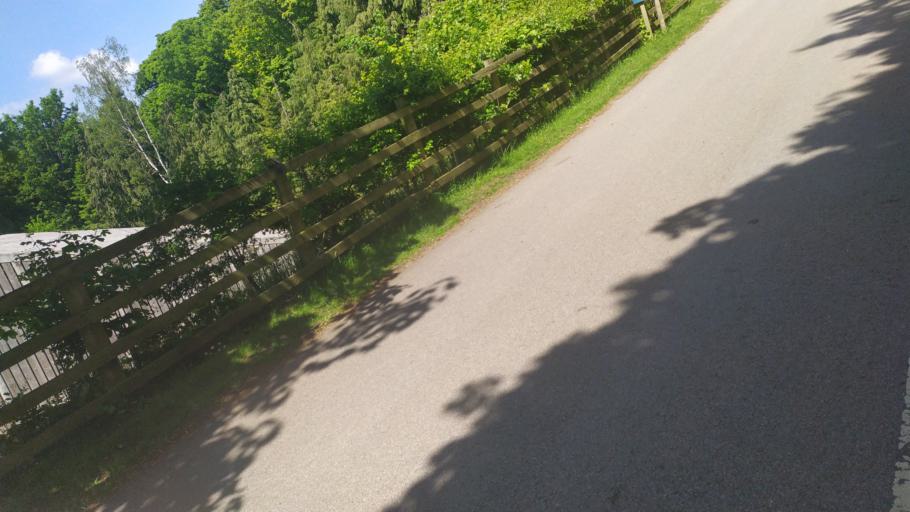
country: GB
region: England
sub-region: North Yorkshire
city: Pannal
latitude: 53.8979
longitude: -1.5355
